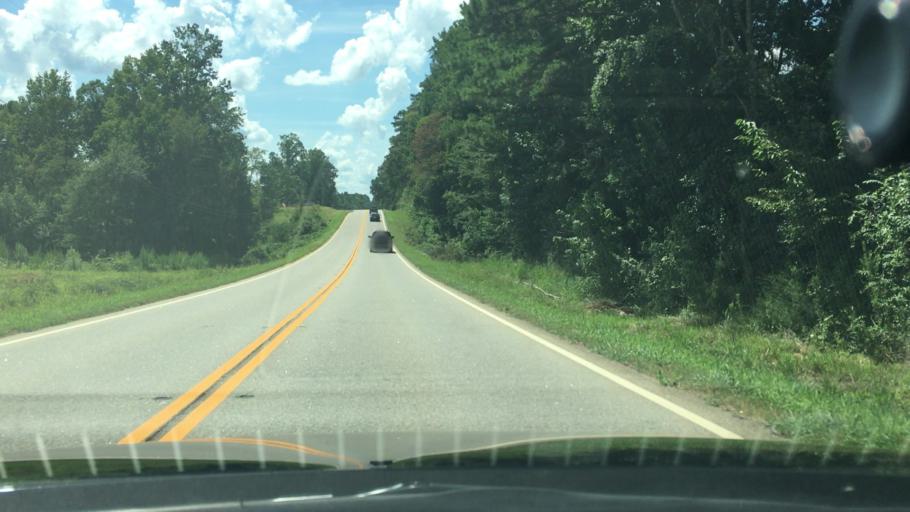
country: US
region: Georgia
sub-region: Putnam County
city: Eatonton
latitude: 33.3079
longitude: -83.4978
